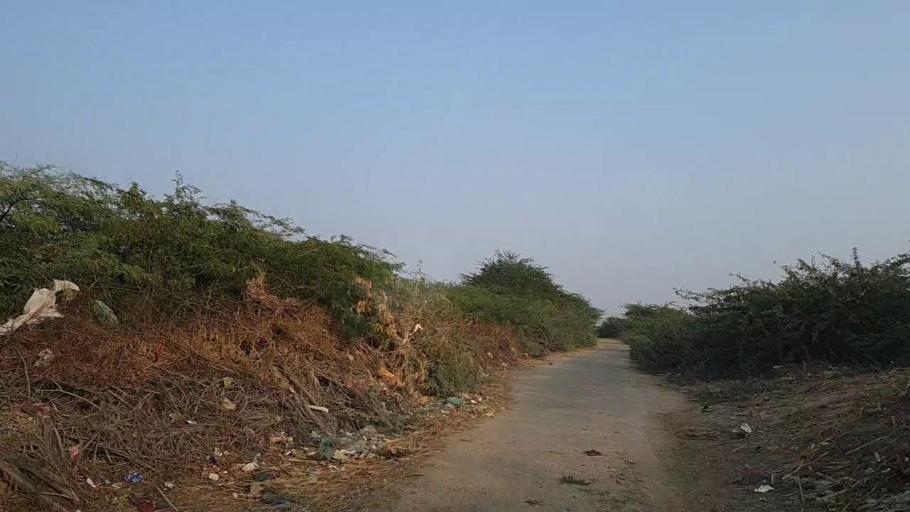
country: PK
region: Sindh
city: Thatta
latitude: 24.6897
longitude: 67.8179
